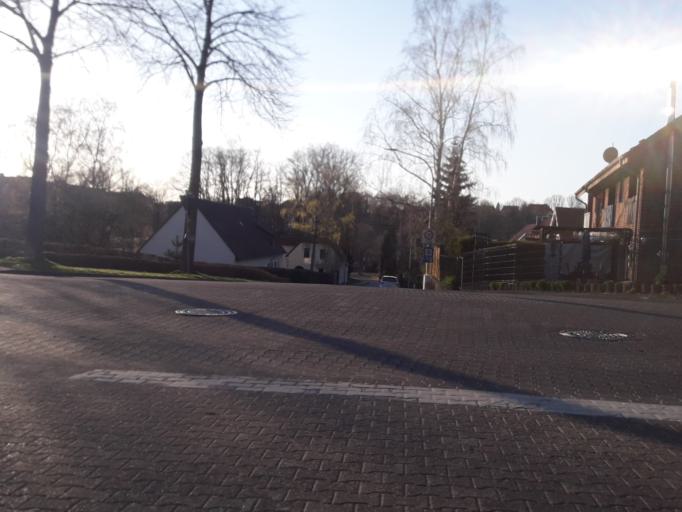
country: DE
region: North Rhine-Westphalia
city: Bad Lippspringe
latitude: 51.7460
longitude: 8.8575
